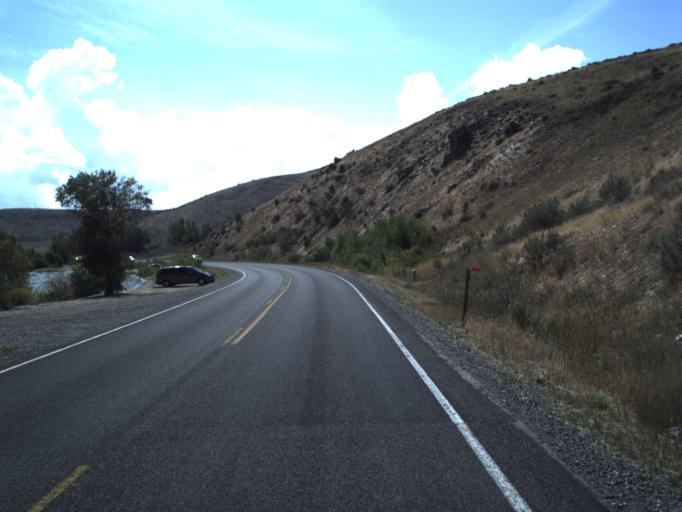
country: US
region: Utah
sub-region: Rich County
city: Randolph
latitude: 41.8622
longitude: -111.3653
